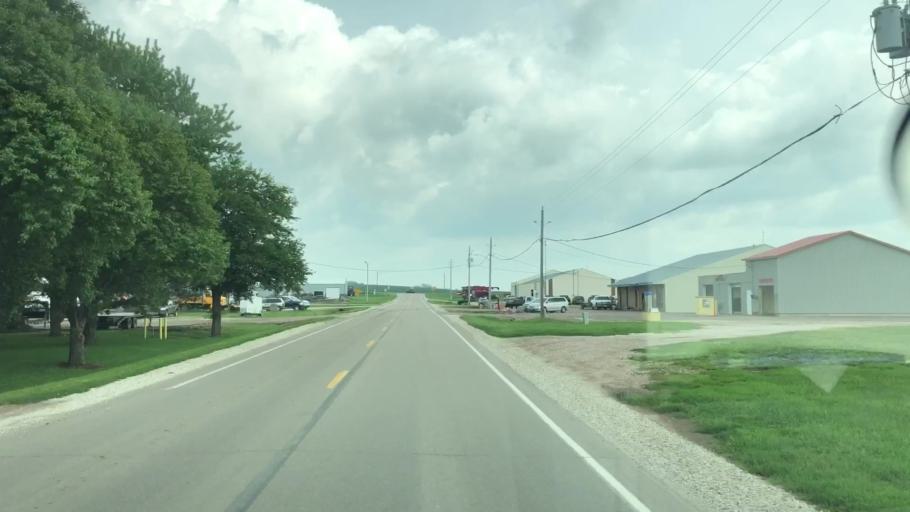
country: US
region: Iowa
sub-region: Plymouth County
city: Kingsley
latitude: 42.5866
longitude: -95.9618
